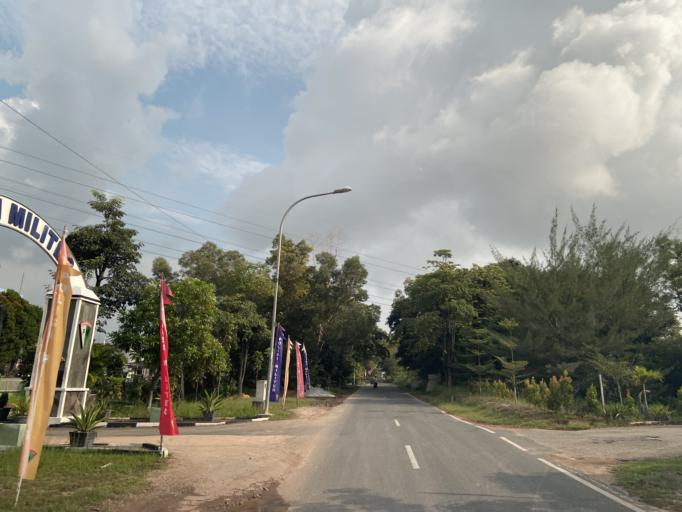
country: SG
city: Singapore
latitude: 1.1151
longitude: 104.0223
